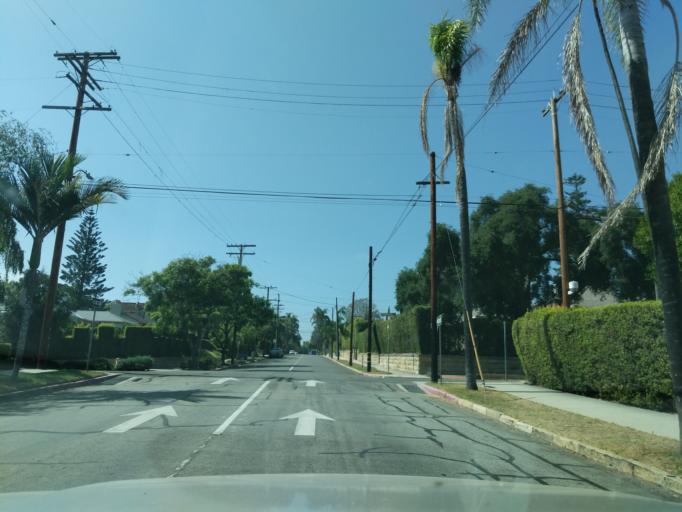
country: US
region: California
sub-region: Santa Barbara County
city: Santa Barbara
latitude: 34.4319
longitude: -119.7109
